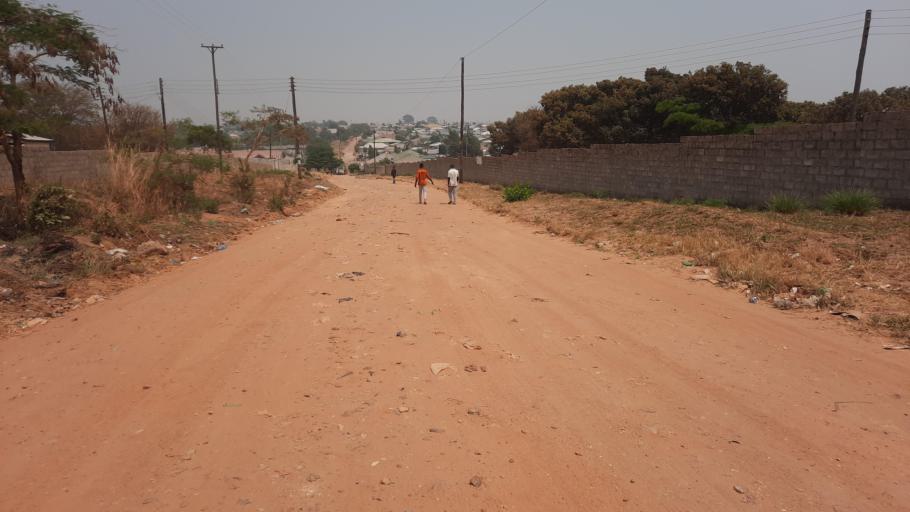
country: ZM
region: Lusaka
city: Lusaka
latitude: -15.4105
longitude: 28.3784
